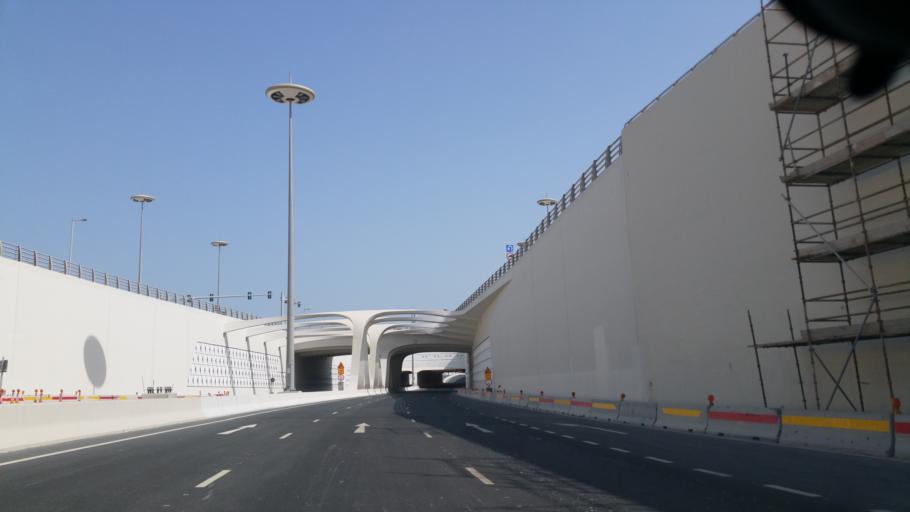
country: QA
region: Baladiyat Umm Salal
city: Umm Salal Muhammad
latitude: 25.4093
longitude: 51.5110
